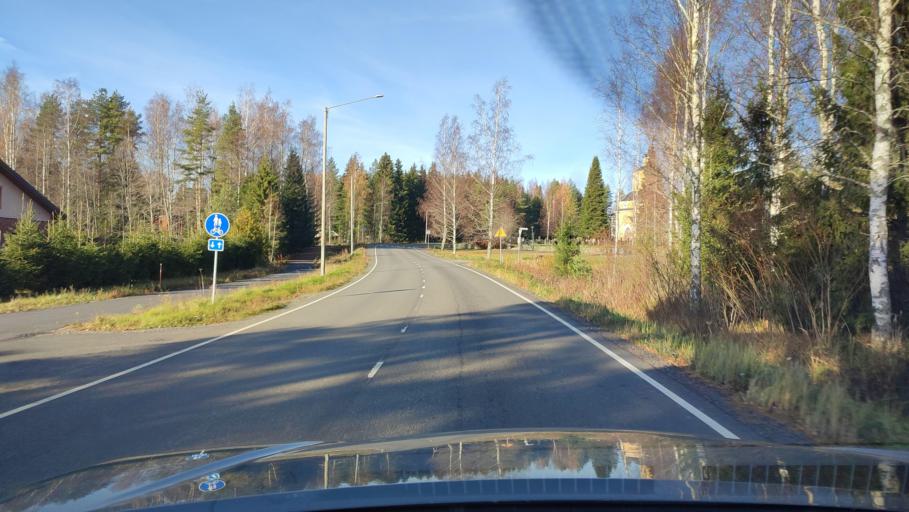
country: FI
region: Southern Ostrobothnia
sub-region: Suupohja
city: Karijoki
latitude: 62.3105
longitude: 21.7080
